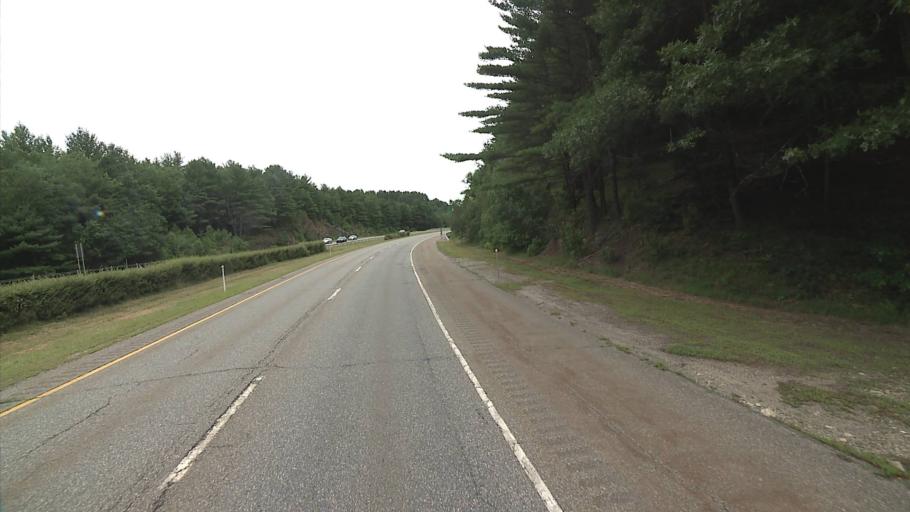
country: US
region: Connecticut
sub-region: Litchfield County
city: Northwest Harwinton
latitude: 41.7557
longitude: -73.1148
